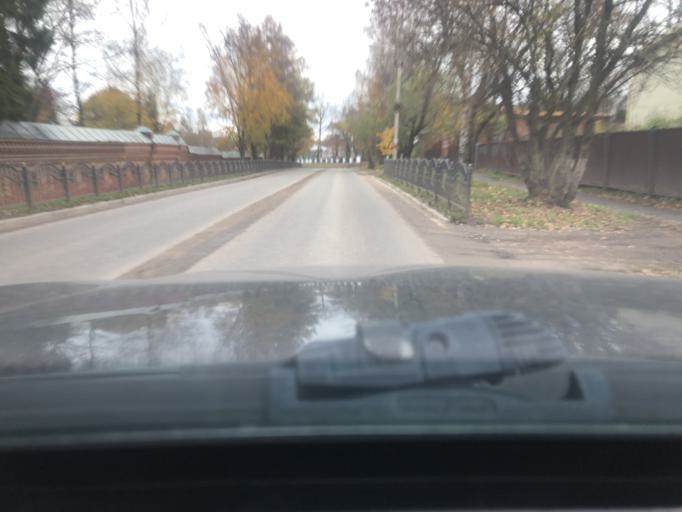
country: RU
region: Moskovskaya
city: Sergiyev Posad
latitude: 56.3088
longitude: 38.1255
